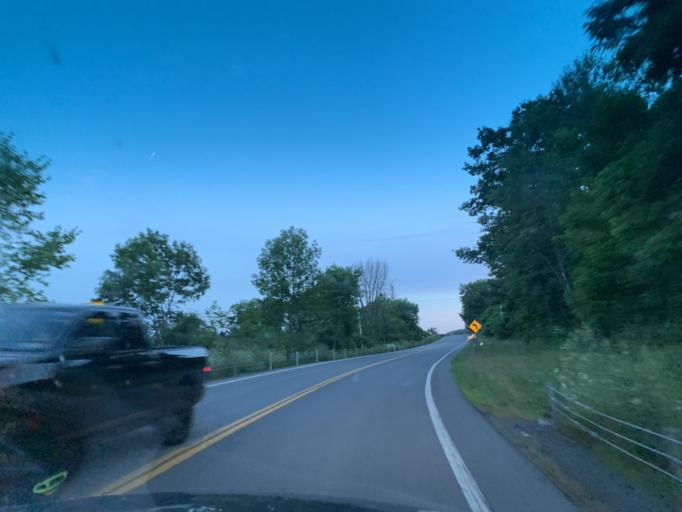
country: US
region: New York
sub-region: Chenango County
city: New Berlin
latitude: 42.6543
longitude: -75.3310
